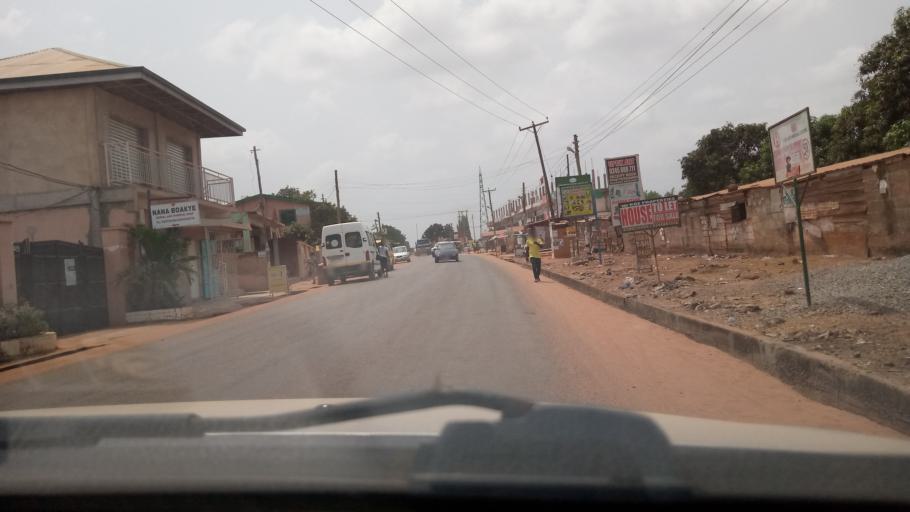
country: GH
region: Greater Accra
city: Dome
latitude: 5.6693
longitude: -0.2056
